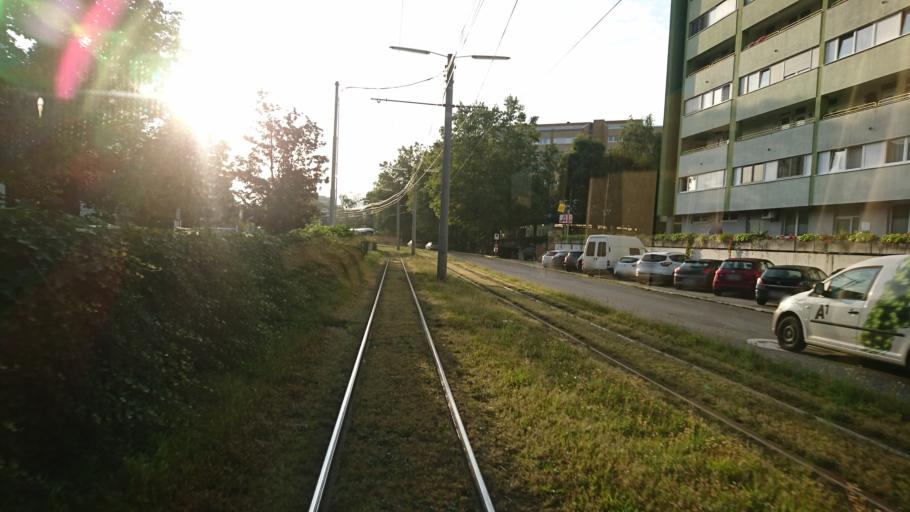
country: AT
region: Upper Austria
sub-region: Linz Stadt
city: Linz
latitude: 48.3321
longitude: 14.3108
